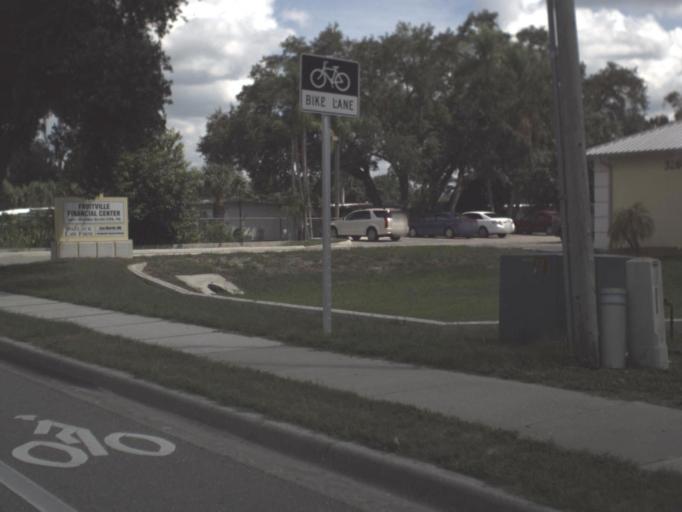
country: US
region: Florida
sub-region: Sarasota County
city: Kensington Park
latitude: 27.3374
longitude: -82.5045
